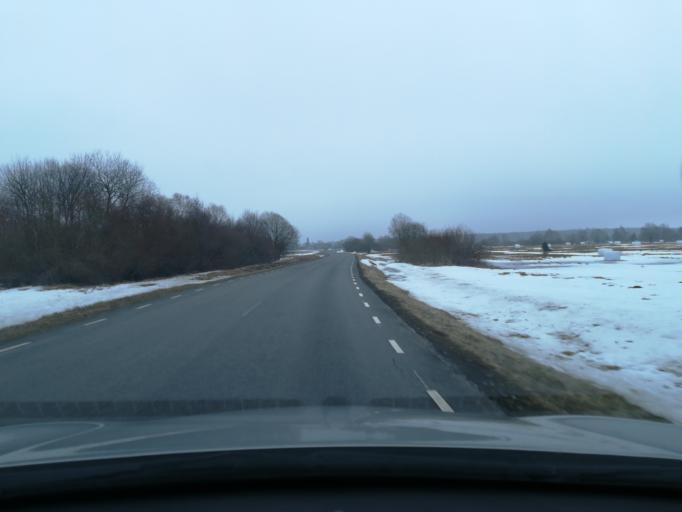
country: EE
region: Harju
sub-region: Kuusalu vald
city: Kuusalu
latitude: 59.4734
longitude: 25.5488
